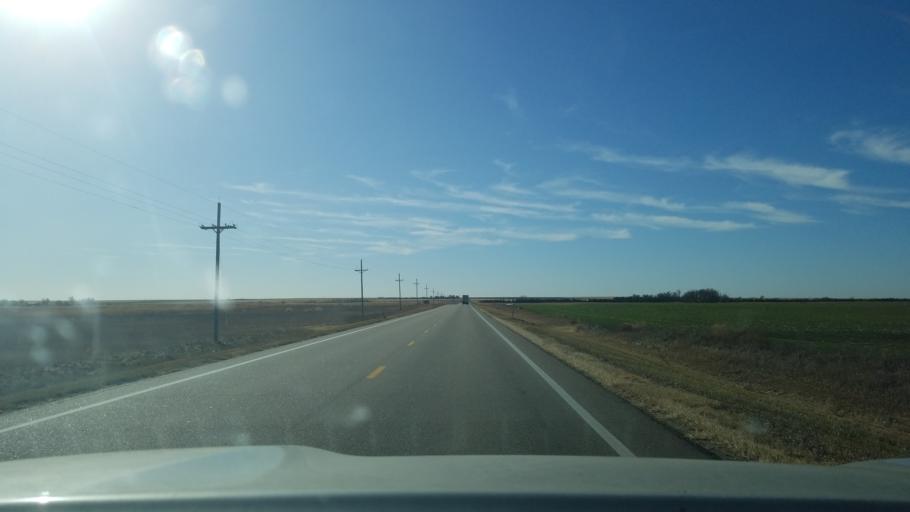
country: US
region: Kansas
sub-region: Ness County
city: Ness City
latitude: 38.4212
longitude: -99.8986
